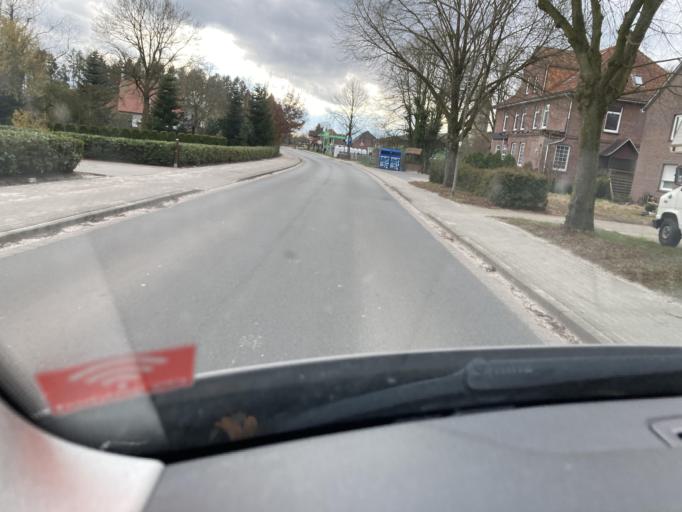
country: DE
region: Lower Saxony
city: Zetel
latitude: 53.4439
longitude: 7.9383
